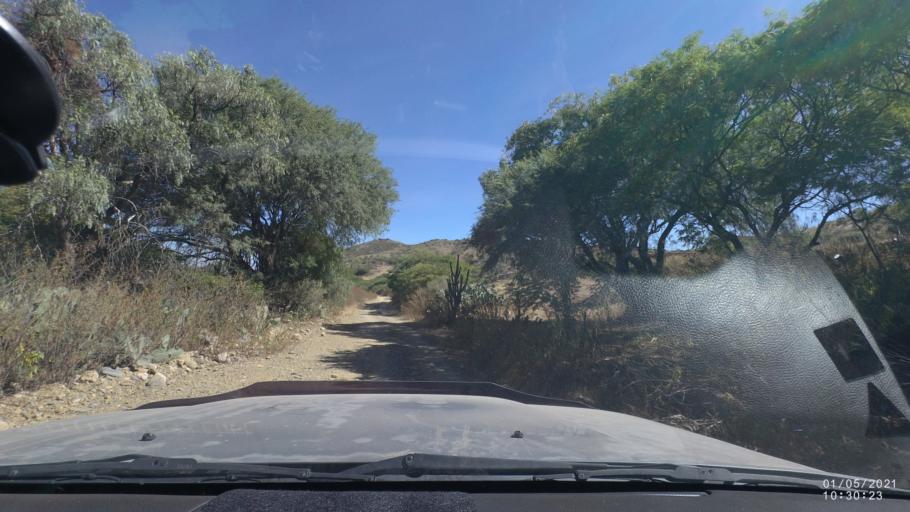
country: BO
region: Cochabamba
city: Capinota
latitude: -17.5935
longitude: -66.1913
